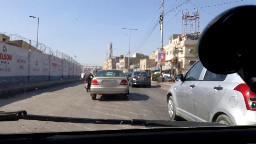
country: PK
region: Sindh
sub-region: Karachi District
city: Karachi
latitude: 24.8996
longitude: 67.1068
